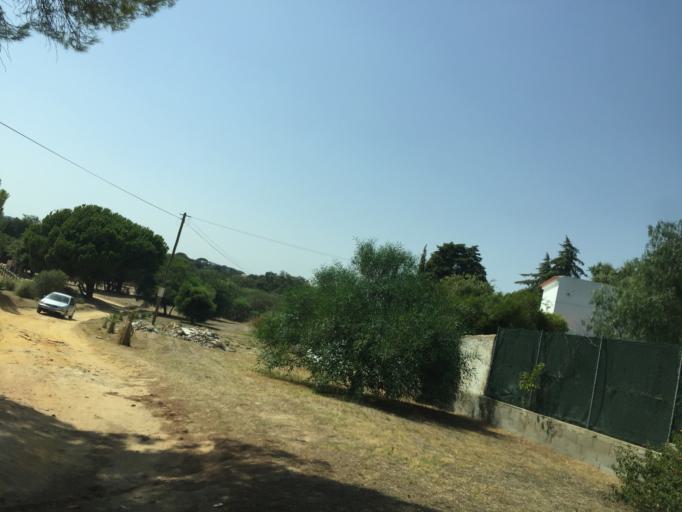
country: PT
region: Faro
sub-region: Albufeira
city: Ferreiras
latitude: 37.1035
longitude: -8.2021
